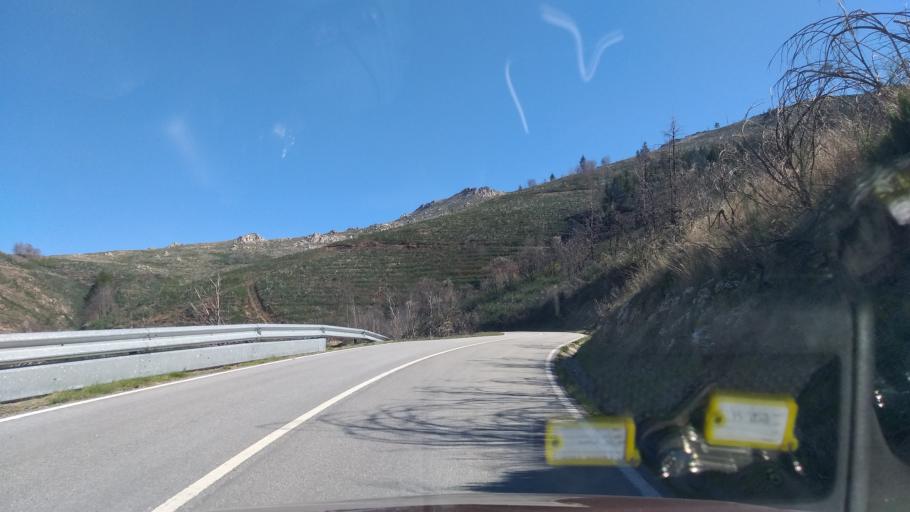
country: PT
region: Guarda
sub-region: Manteigas
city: Manteigas
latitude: 40.4856
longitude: -7.5562
